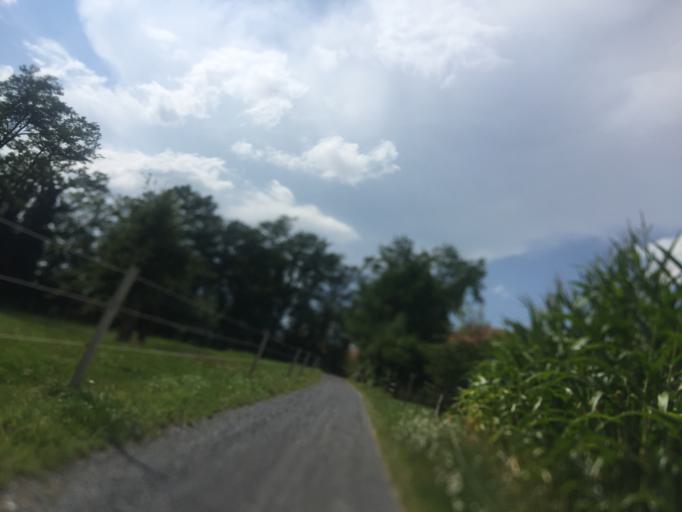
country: CH
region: Bern
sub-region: Bern-Mittelland District
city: Rubigen
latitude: 46.9017
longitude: 7.5334
